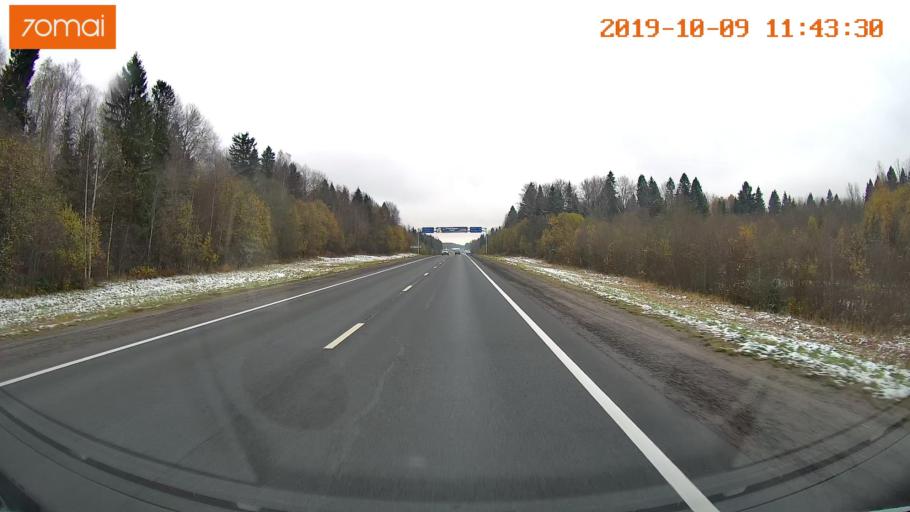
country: RU
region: Vologda
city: Gryazovets
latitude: 58.8961
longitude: 40.1858
